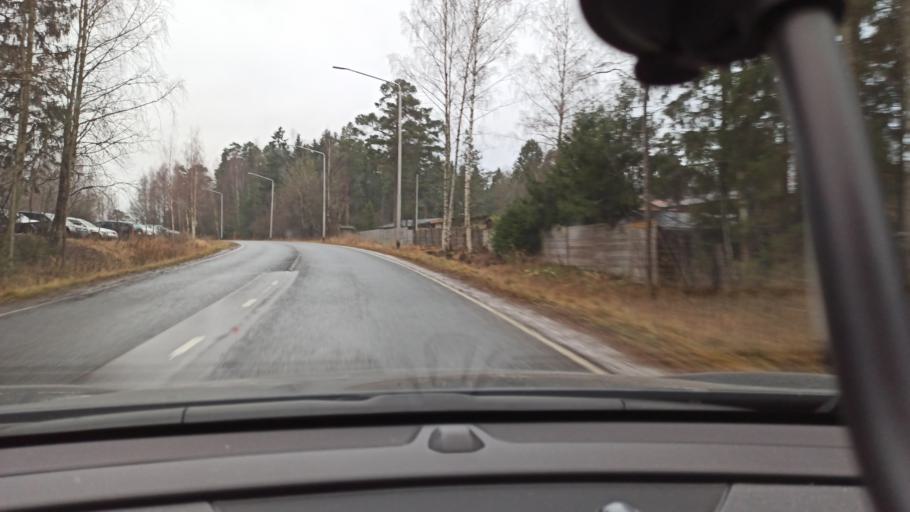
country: FI
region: Uusimaa
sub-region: Helsinki
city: Kirkkonummi
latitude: 60.1389
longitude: 24.4492
